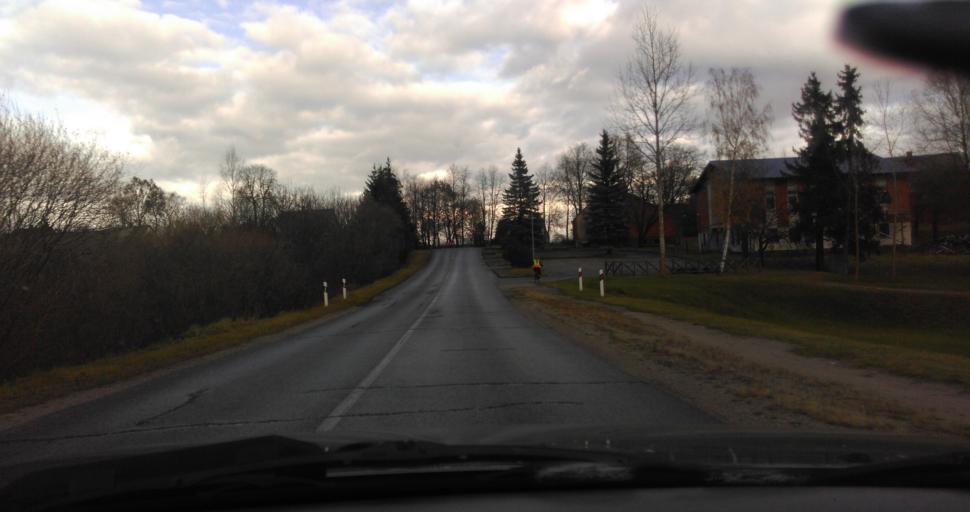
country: LT
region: Utenos apskritis
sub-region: Utena
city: Utena
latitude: 55.5783
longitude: 25.4945
